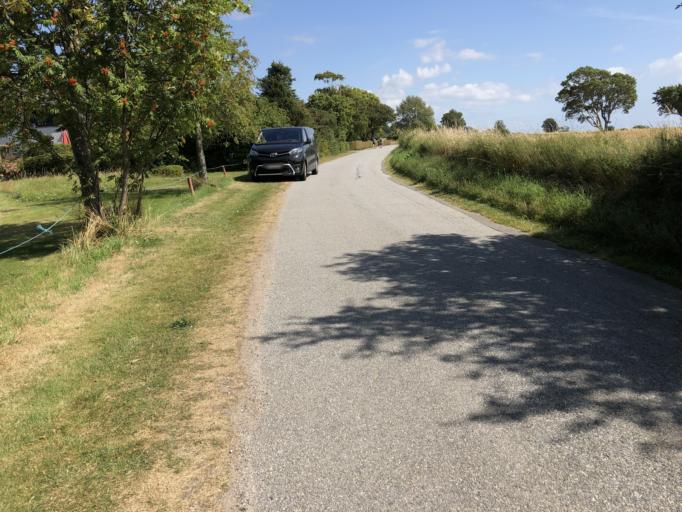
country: DK
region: South Denmark
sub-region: AEro Kommune
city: AEroskobing
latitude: 54.8974
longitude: 10.2863
